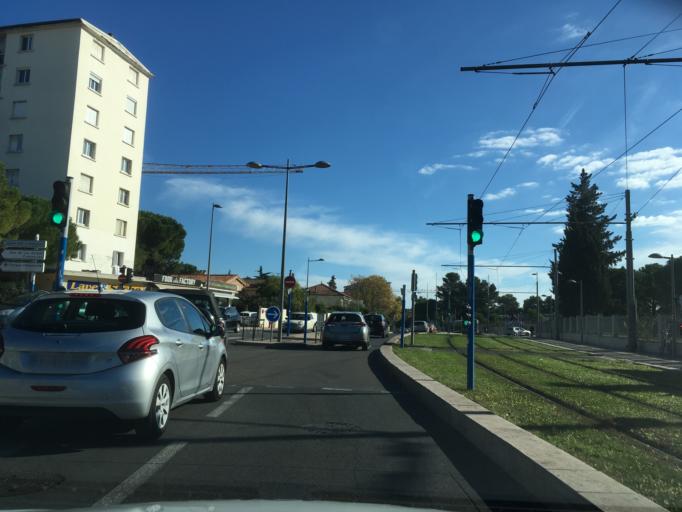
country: FR
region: Languedoc-Roussillon
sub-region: Departement de l'Herault
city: Montpellier
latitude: 43.6123
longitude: 3.8454
